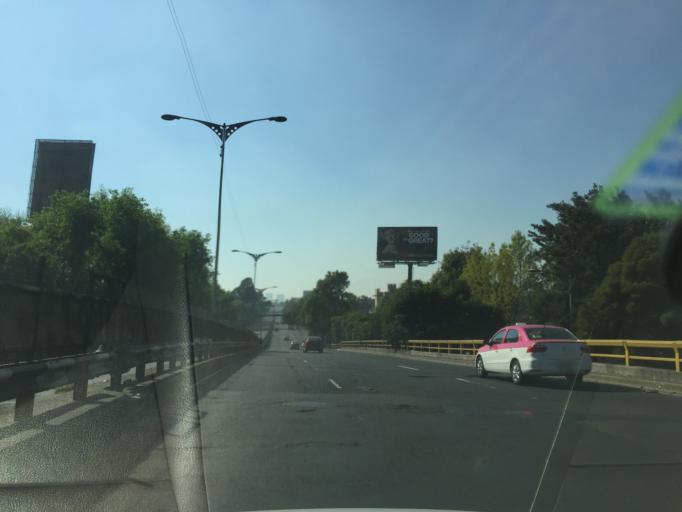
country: MX
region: Mexico City
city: Azcapotzalco
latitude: 19.4698
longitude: -99.1896
